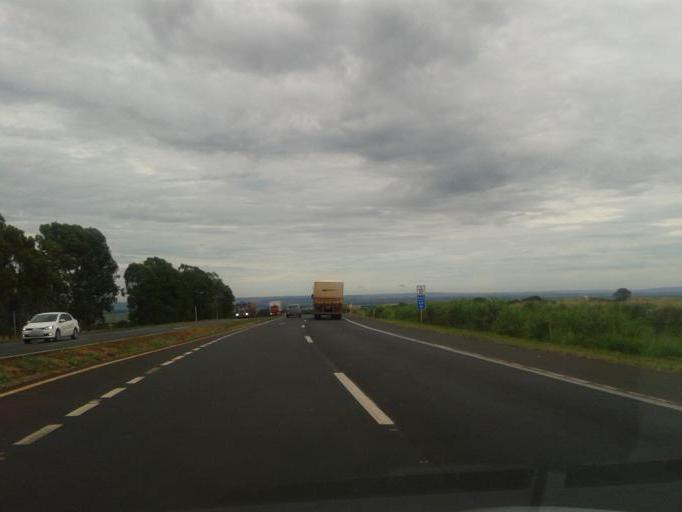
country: BR
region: Minas Gerais
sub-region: Centralina
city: Centralina
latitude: -18.6383
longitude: -49.1795
